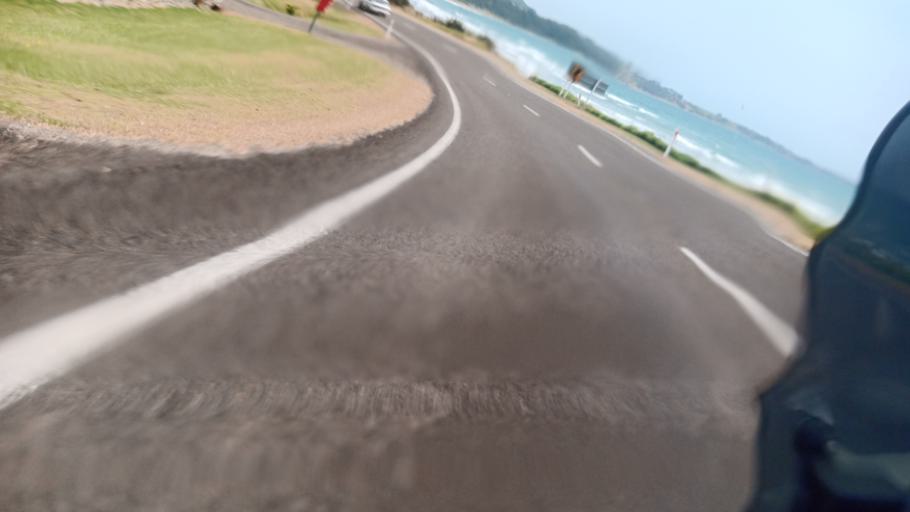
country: NZ
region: Bay of Plenty
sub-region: Opotiki District
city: Opotiki
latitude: -37.6102
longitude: 177.9592
